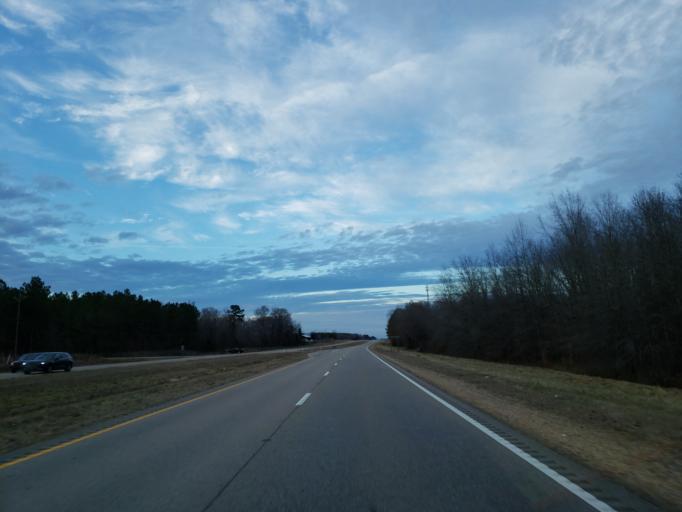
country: US
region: Mississippi
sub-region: Kemper County
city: De Kalb
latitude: 32.7627
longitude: -88.4648
